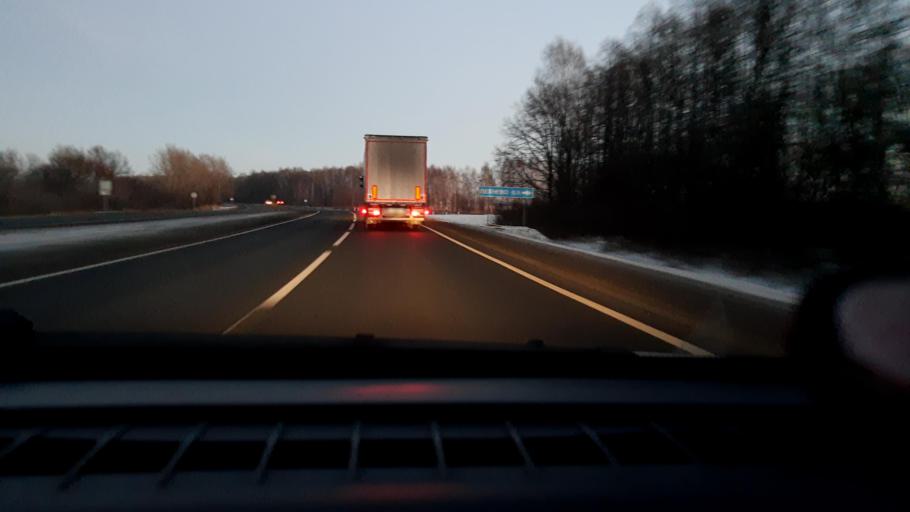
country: RU
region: Nizjnij Novgorod
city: Lyskovo
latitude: 56.0089
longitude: 44.9353
